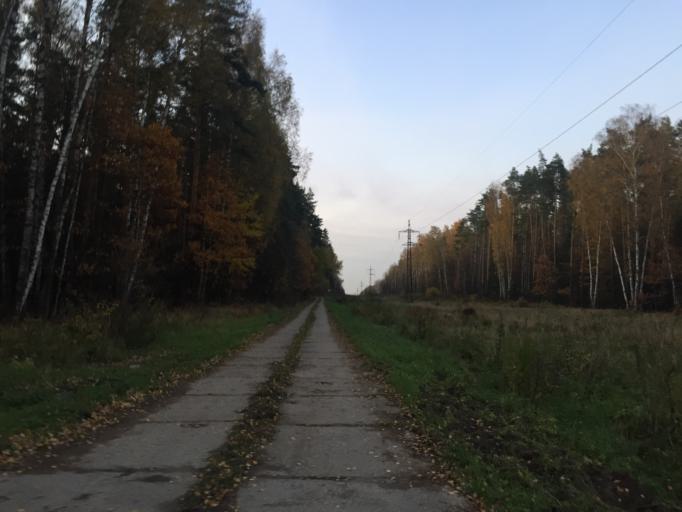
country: RU
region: Moskovskaya
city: Druzhba
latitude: 55.8655
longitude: 37.7678
